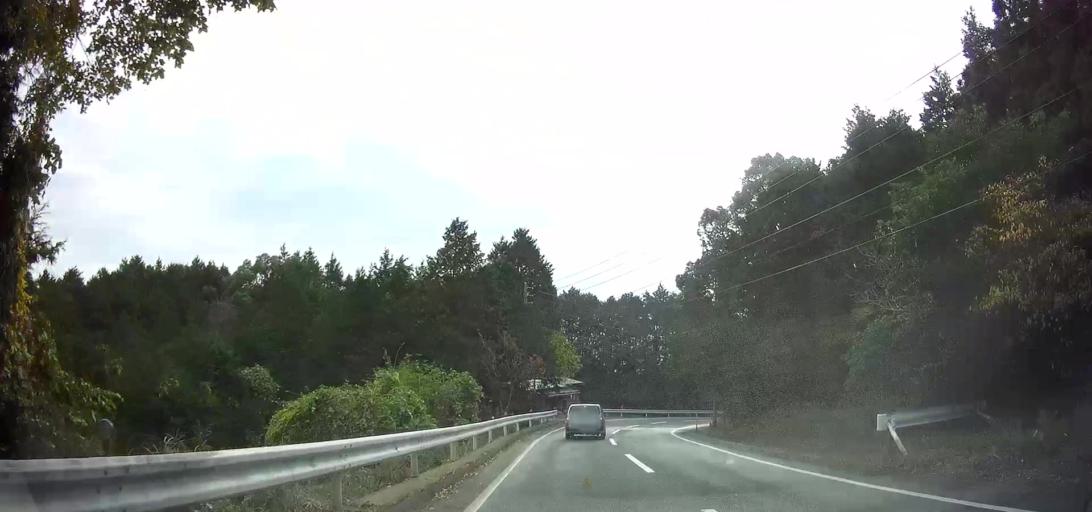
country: JP
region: Nagasaki
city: Shimabara
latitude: 32.6931
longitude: 130.2562
